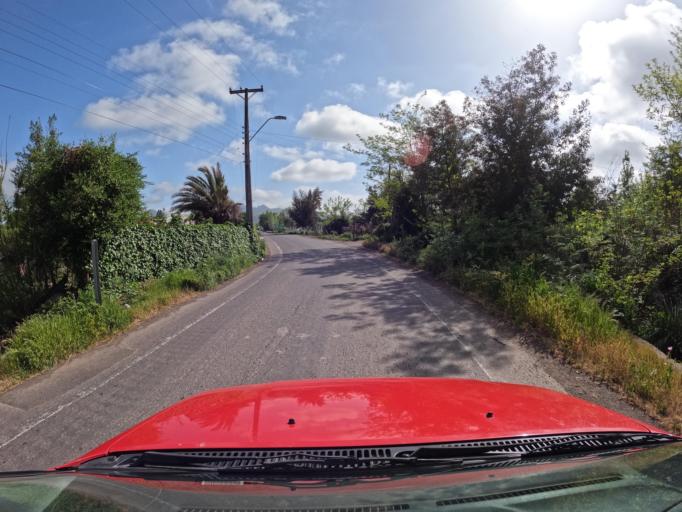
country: CL
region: Maule
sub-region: Provincia de Curico
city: Teno
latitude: -34.8816
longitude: -71.2259
